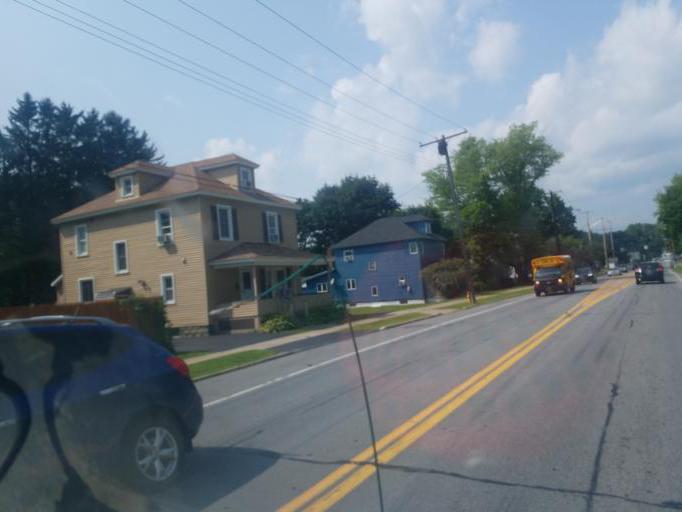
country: US
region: New York
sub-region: Fulton County
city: Johnstown
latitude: 43.0058
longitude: -74.3592
